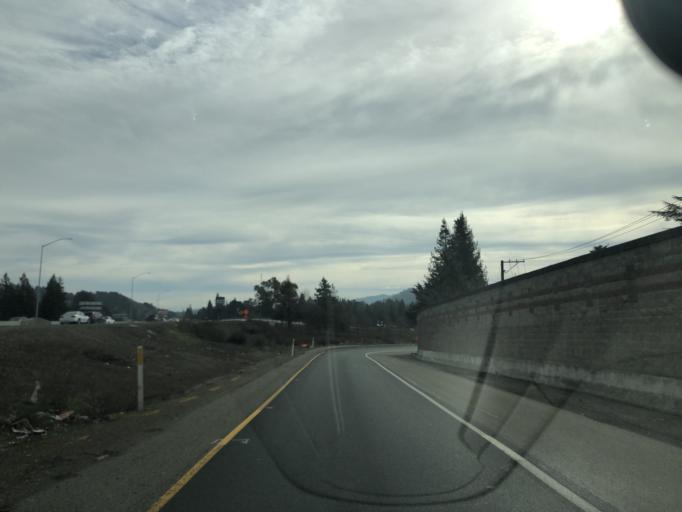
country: US
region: California
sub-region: Contra Costa County
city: Saranap
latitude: 37.8873
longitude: -122.0569
